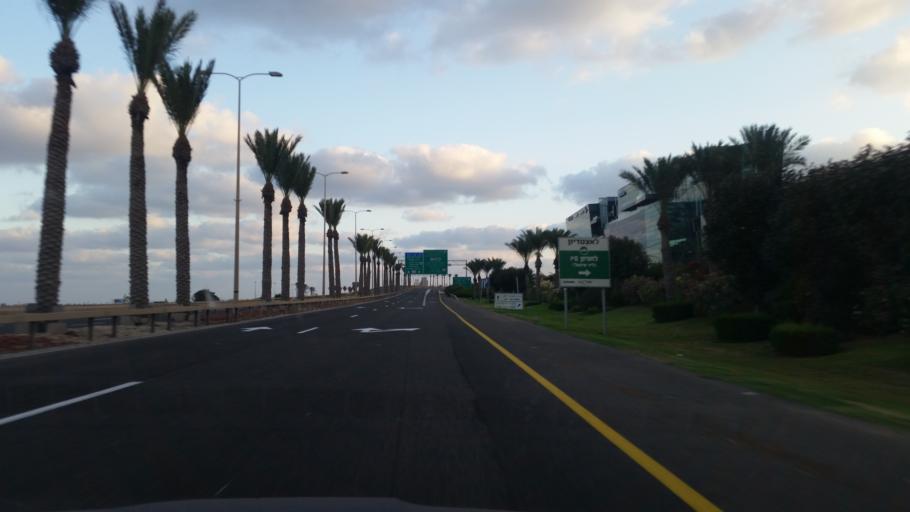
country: IL
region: Haifa
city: Tirat Karmel
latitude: 32.7858
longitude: 34.9566
